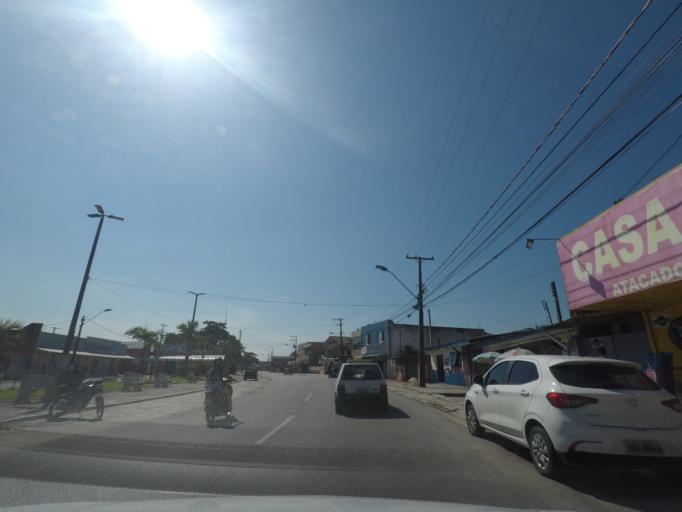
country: BR
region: Parana
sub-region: Guaratuba
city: Guaratuba
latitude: -25.8148
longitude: -48.5339
